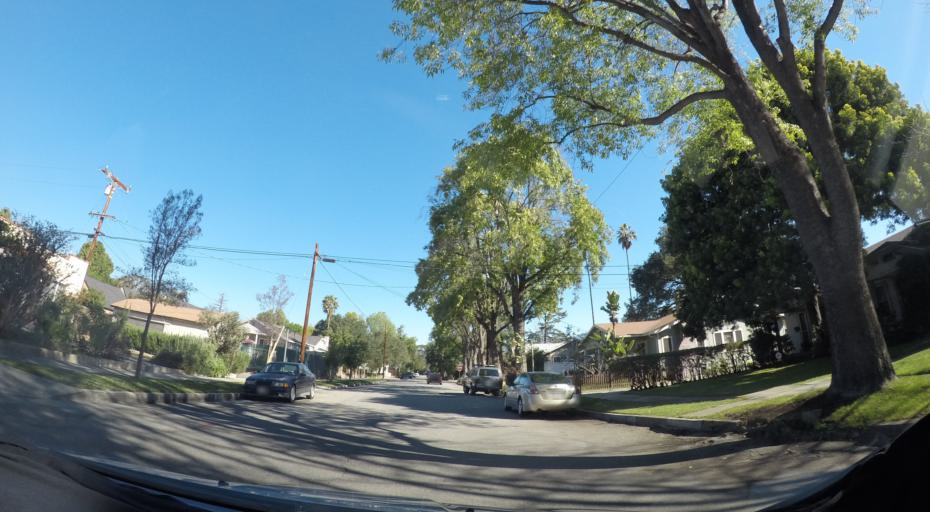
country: US
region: California
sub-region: Los Angeles County
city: South Pasadena
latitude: 34.1133
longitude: -118.1650
